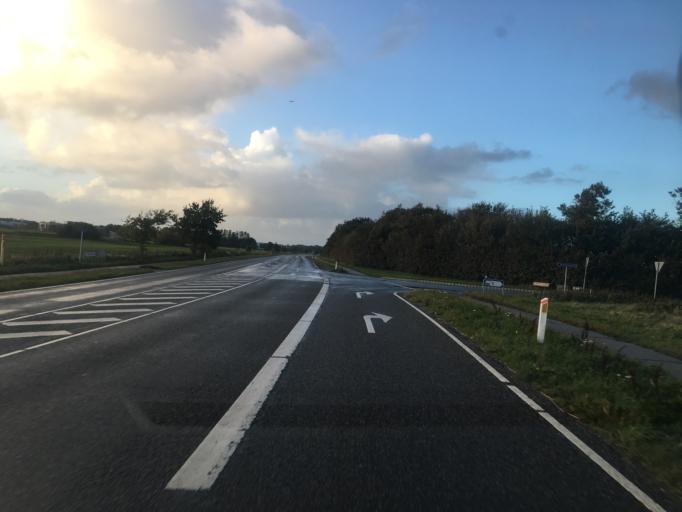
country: DK
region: South Denmark
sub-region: Tonder Kommune
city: Tonder
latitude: 54.9294
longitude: 8.8497
